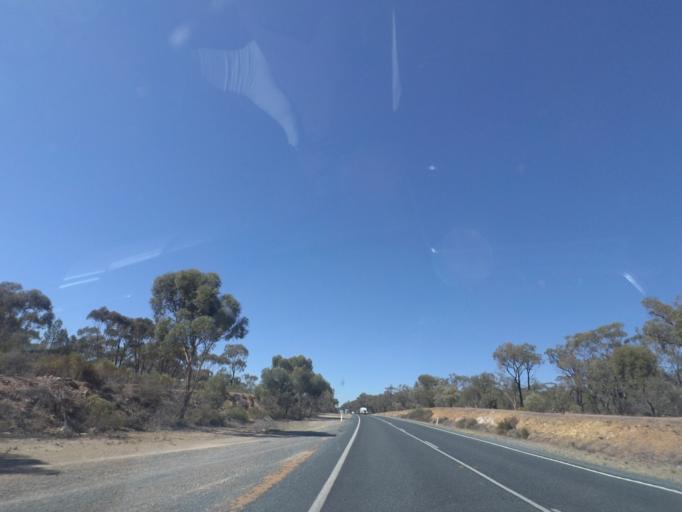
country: AU
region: New South Wales
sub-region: Bland
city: West Wyalong
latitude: -34.1382
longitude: 147.1209
